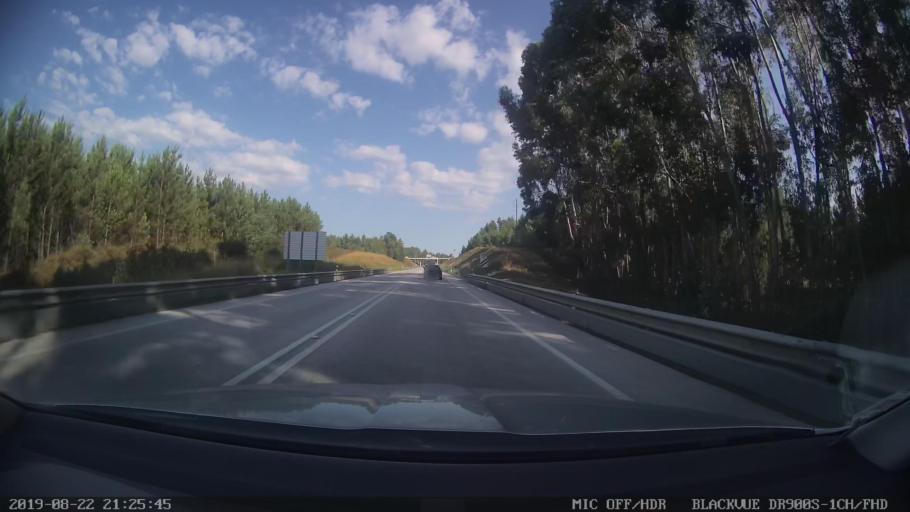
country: PT
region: Castelo Branco
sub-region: Serta
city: Serta
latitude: 39.8582
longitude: -8.1269
